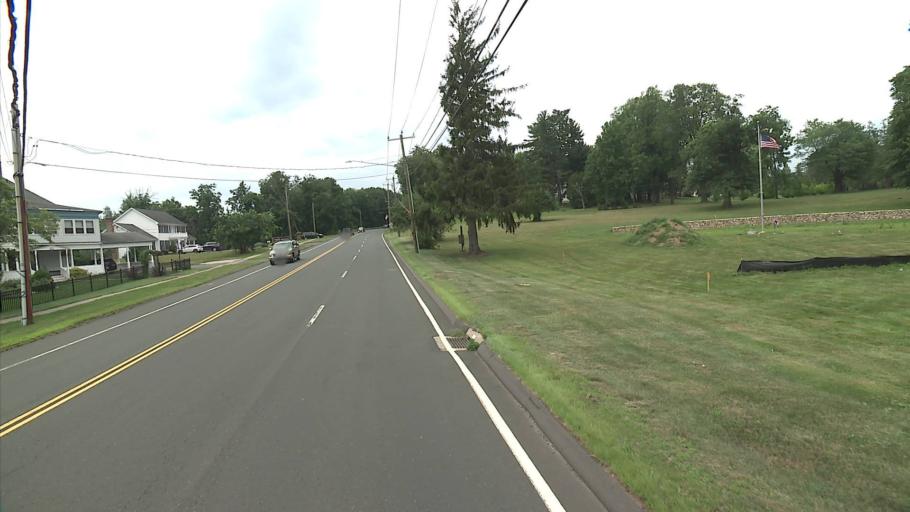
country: US
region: Connecticut
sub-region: Middlesex County
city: Cromwell
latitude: 41.6051
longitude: -72.6477
